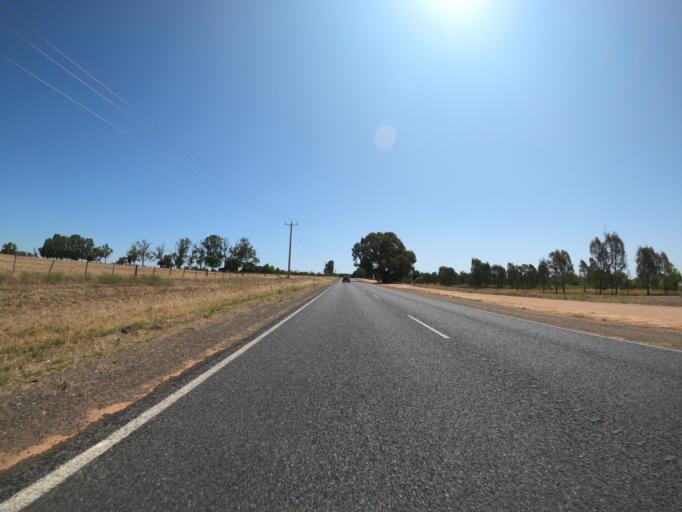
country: AU
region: Victoria
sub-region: Moira
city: Yarrawonga
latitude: -36.0272
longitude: 146.0805
